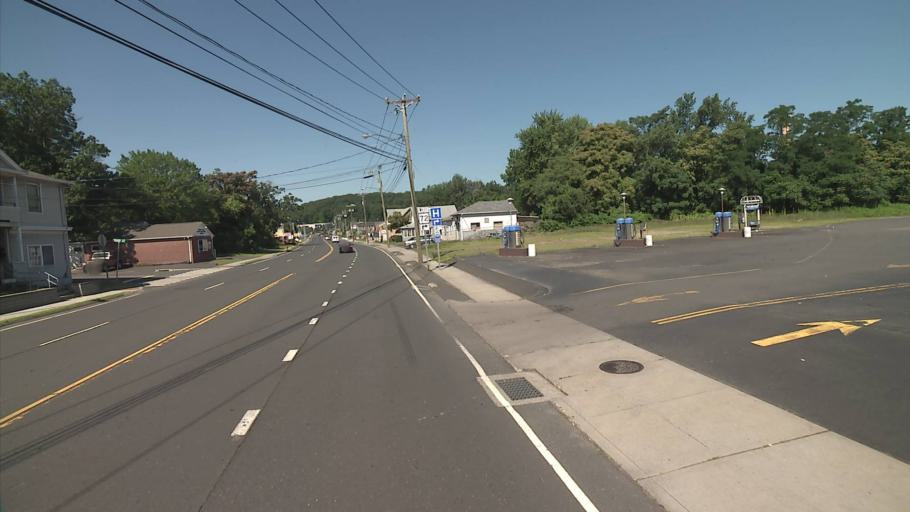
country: US
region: Connecticut
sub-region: Hartford County
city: Bristol
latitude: 41.6681
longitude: -72.9167
